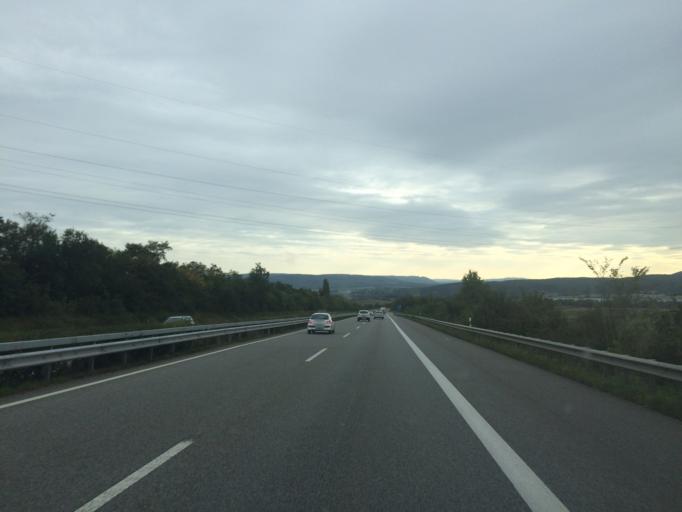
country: DE
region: Rheinland-Pfalz
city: Flussbach
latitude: 50.0010
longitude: 6.9294
